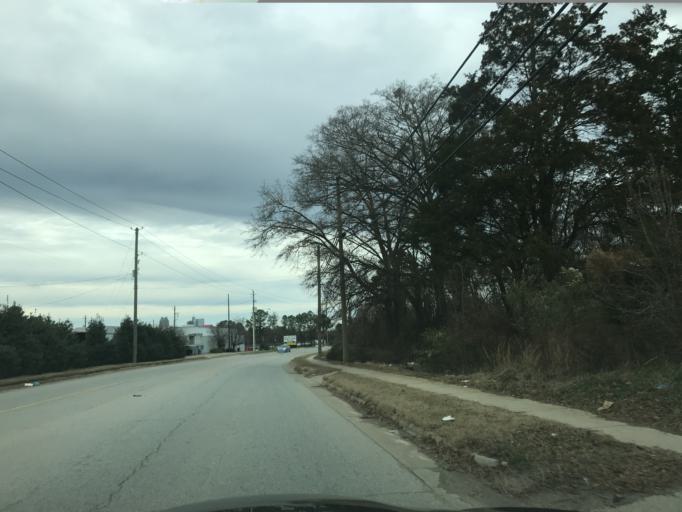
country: US
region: North Carolina
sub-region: Wake County
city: Raleigh
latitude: 35.7480
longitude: -78.6316
